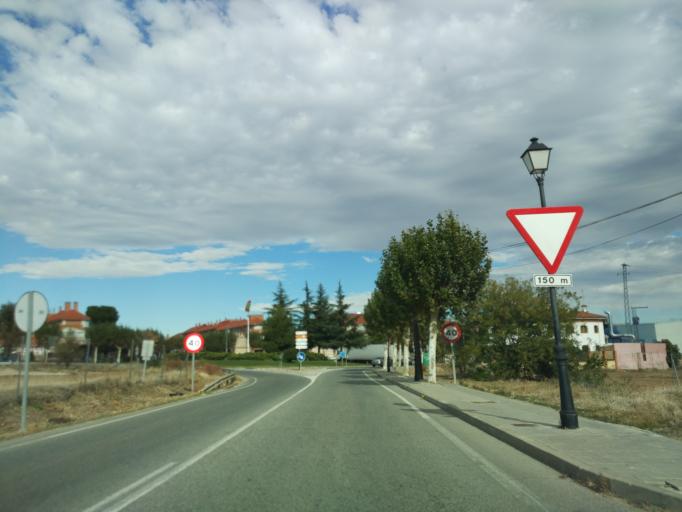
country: ES
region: Madrid
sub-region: Provincia de Madrid
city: Ajalvir
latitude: 40.5295
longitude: -3.4813
